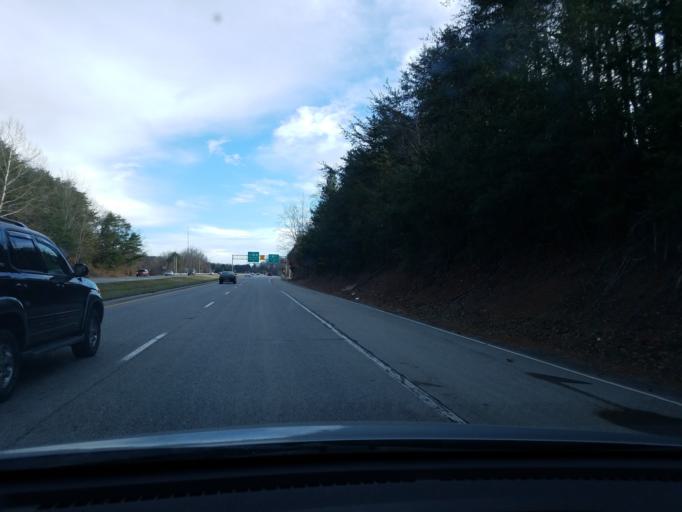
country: US
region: Indiana
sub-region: Floyd County
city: Galena
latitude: 38.3081
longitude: -85.8943
